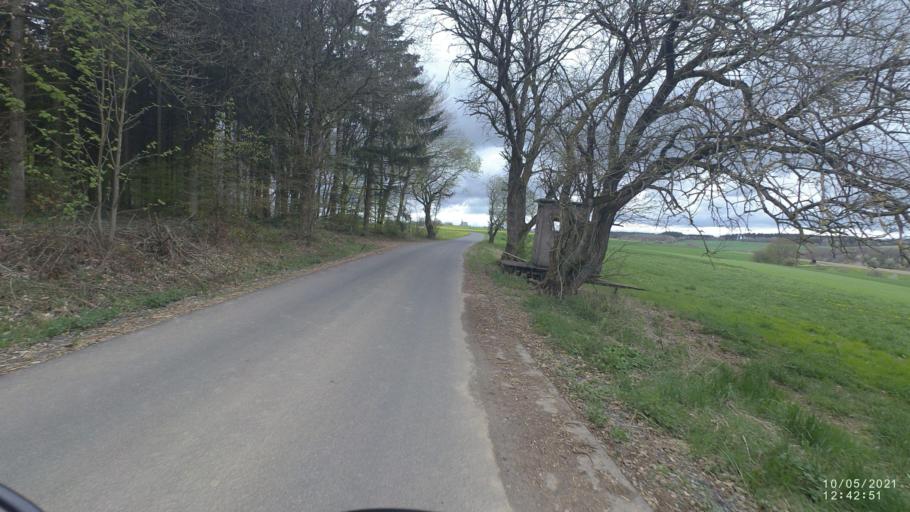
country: DE
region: Rheinland-Pfalz
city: Nachtsheim
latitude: 50.3158
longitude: 7.0799
